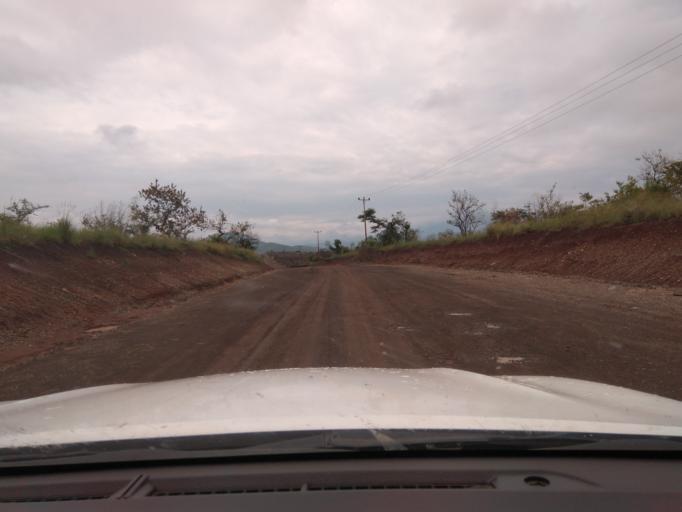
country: ET
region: Southern Nations, Nationalities, and People's Region
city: Felege Neway
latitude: 6.4274
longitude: 37.2581
